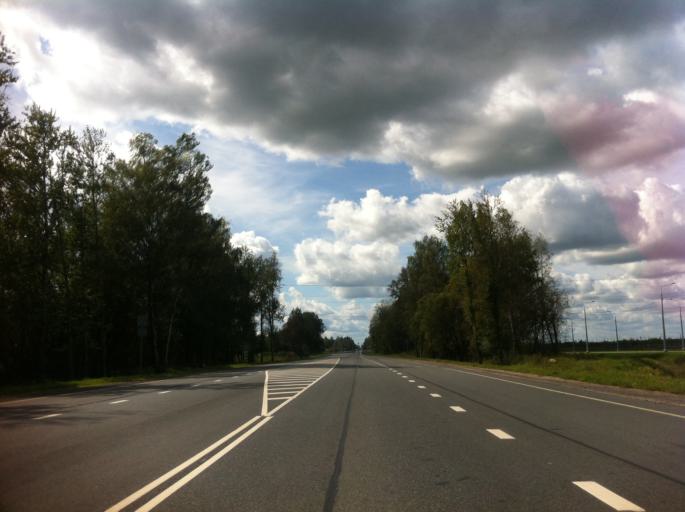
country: RU
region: Pskov
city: Pskov
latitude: 57.7736
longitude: 28.1384
